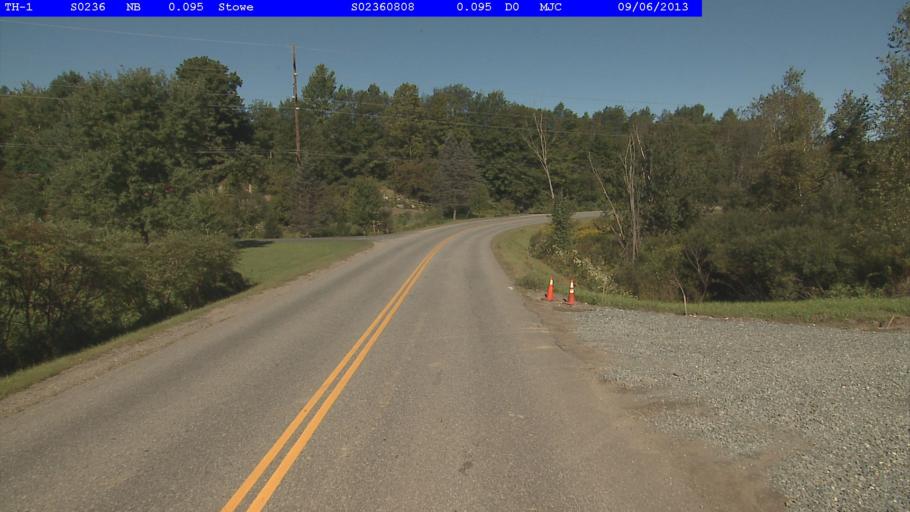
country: US
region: Vermont
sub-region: Washington County
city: Waterbury
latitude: 44.4367
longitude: -72.7131
